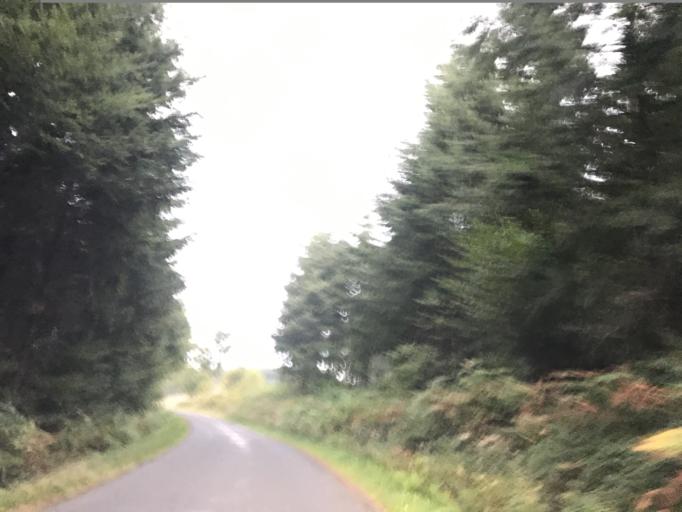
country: FR
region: Auvergne
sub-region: Departement du Puy-de-Dome
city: Celles-sur-Durolle
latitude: 45.8419
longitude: 3.6184
